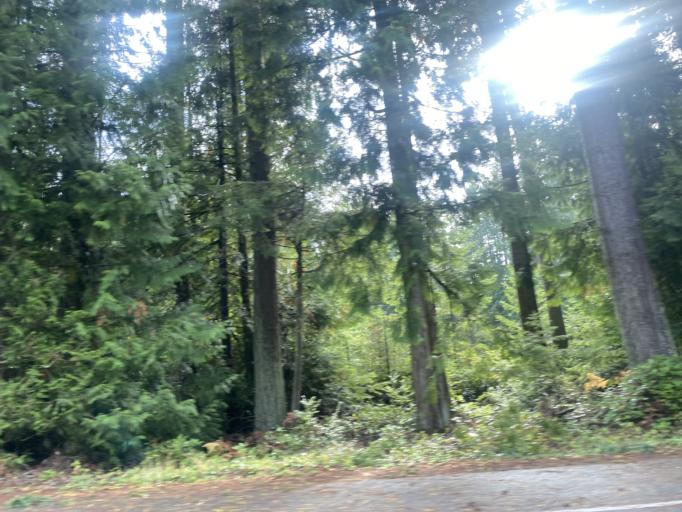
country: US
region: Washington
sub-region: Island County
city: Langley
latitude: 48.0107
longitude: -122.4103
